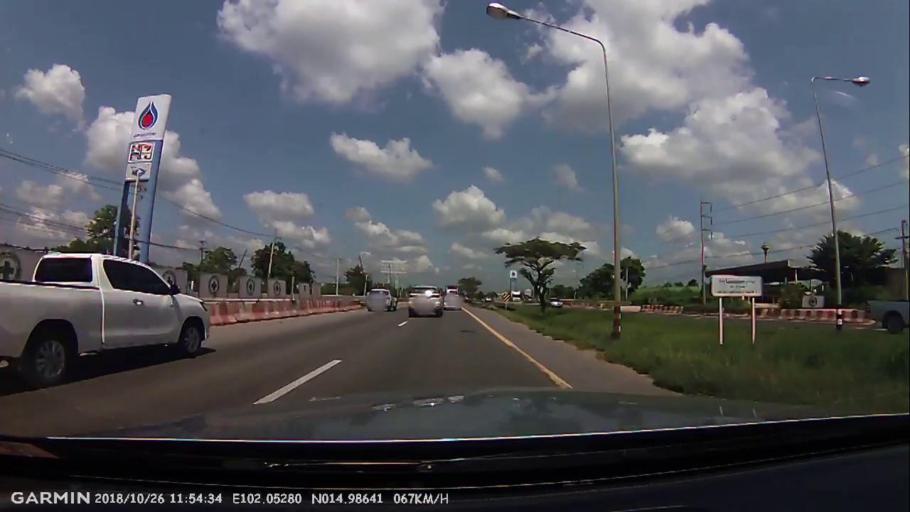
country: TH
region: Nakhon Ratchasima
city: Nakhon Ratchasima
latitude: 14.9865
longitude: 102.0528
